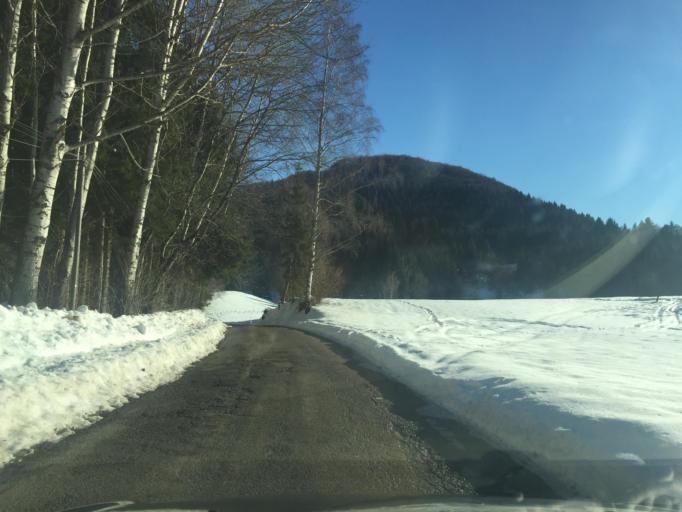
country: IT
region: Friuli Venezia Giulia
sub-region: Provincia di Udine
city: Chiaulis
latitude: 46.4261
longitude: 12.9785
